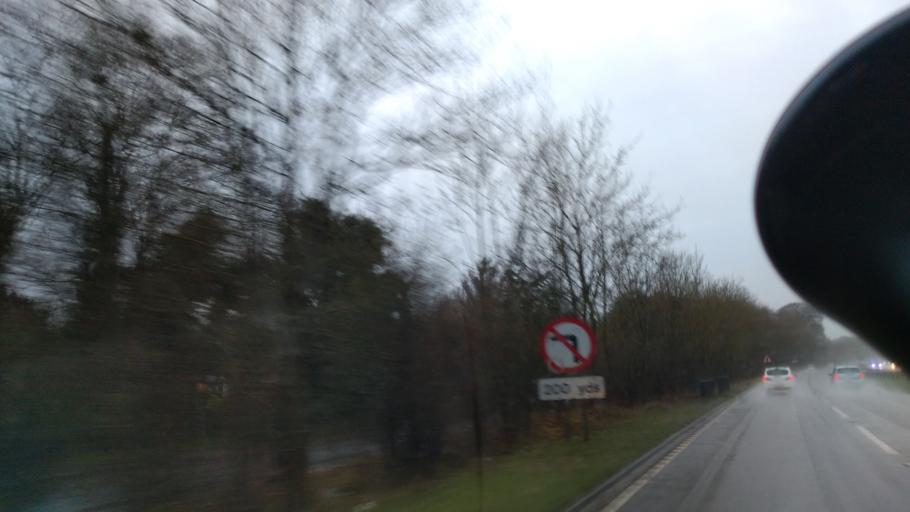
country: GB
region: England
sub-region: East Sussex
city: Lewes
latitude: 50.8652
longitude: -0.0430
